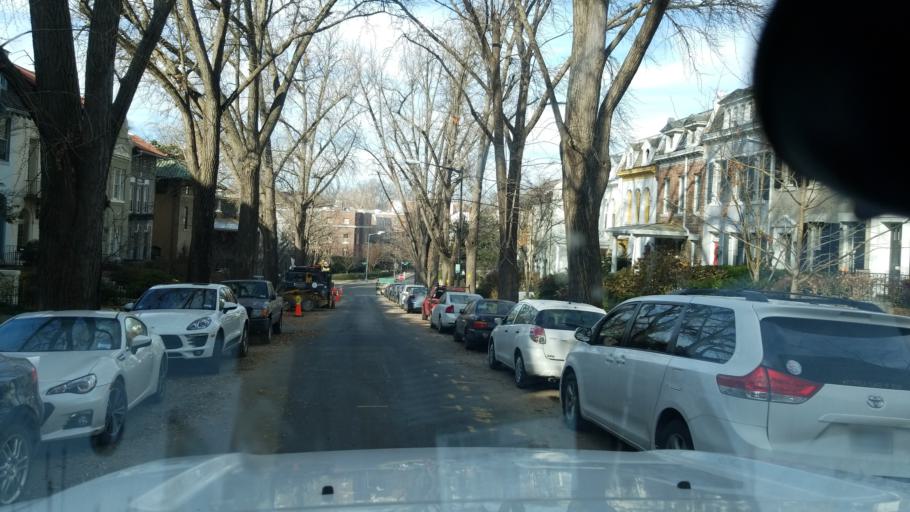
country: US
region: Washington, D.C.
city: Washington, D.C.
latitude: 38.9196
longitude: -77.0464
